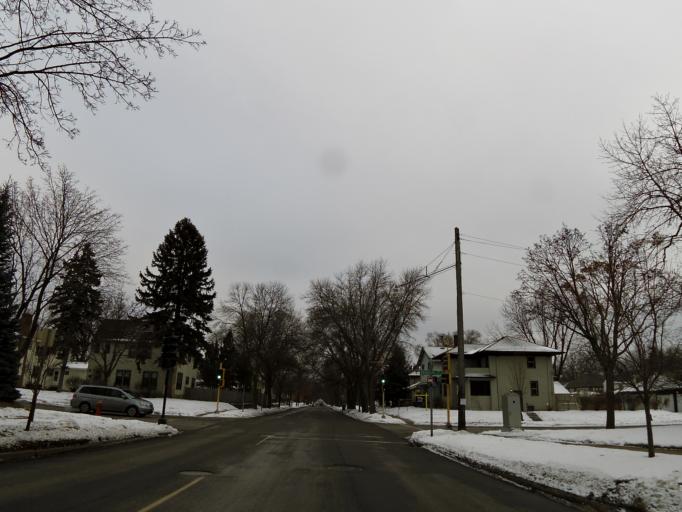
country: US
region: Minnesota
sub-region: Ramsey County
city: Falcon Heights
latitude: 44.9274
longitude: -93.1925
